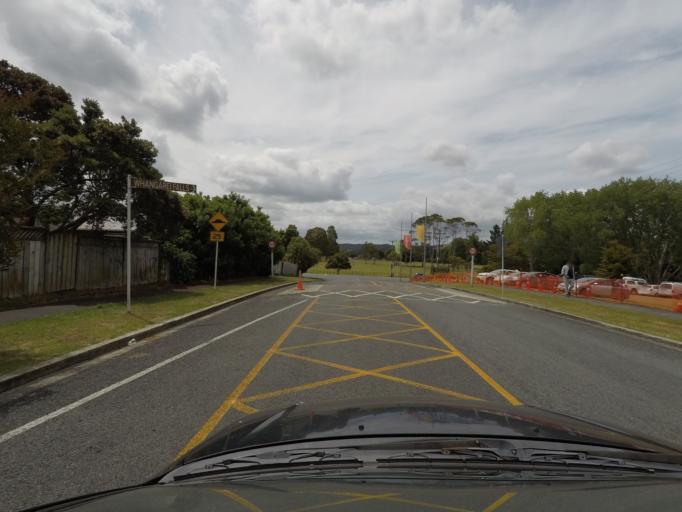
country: NZ
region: Northland
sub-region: Whangarei
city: Whangarei
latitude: -35.6844
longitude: 174.3343
